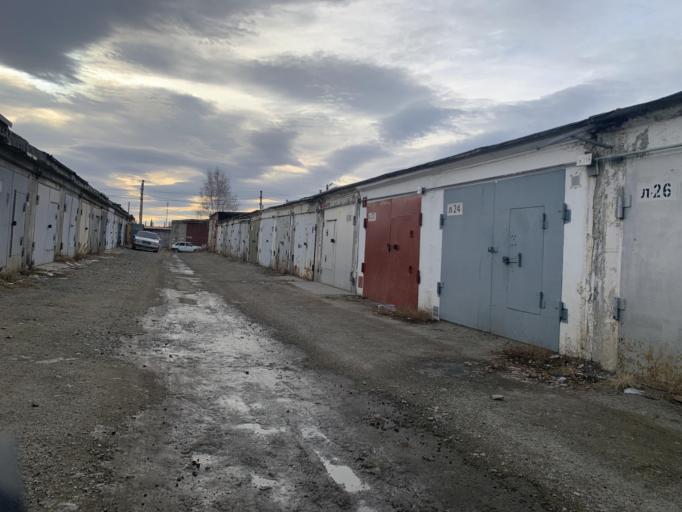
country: RU
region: Chelyabinsk
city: Roshchino
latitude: 55.1950
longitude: 61.2772
